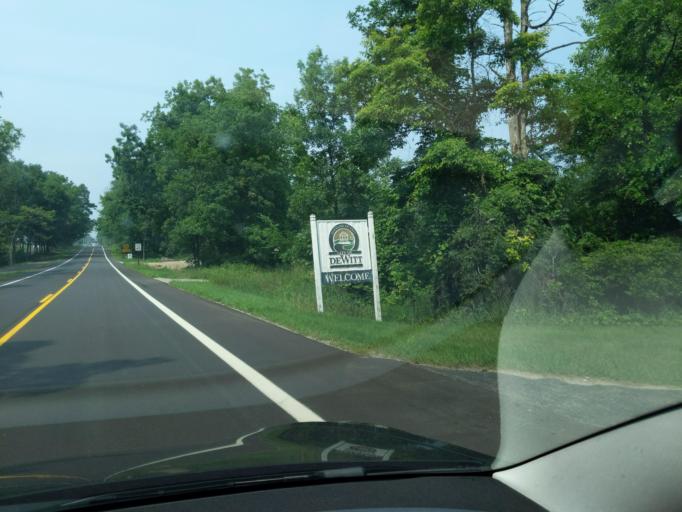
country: US
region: Michigan
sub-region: Clinton County
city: DeWitt
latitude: 42.8208
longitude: -84.5724
